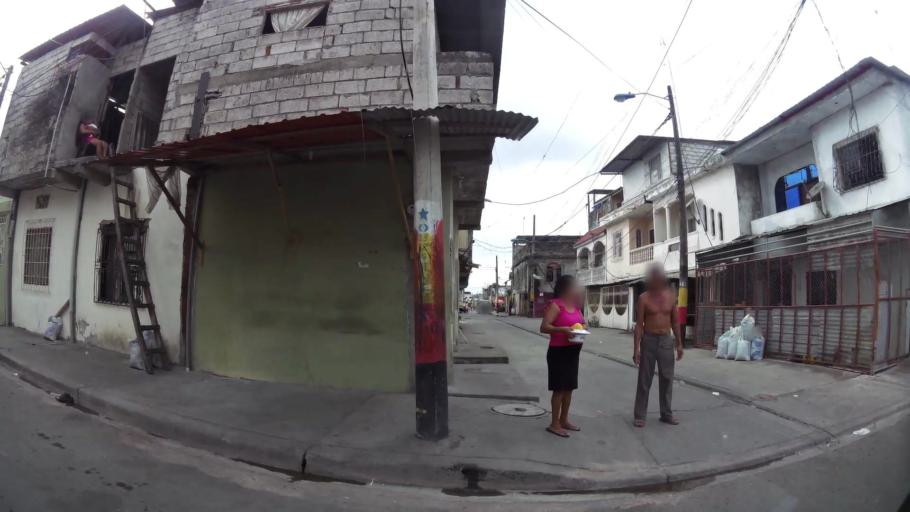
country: EC
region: Guayas
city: Guayaquil
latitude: -2.2349
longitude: -79.9081
